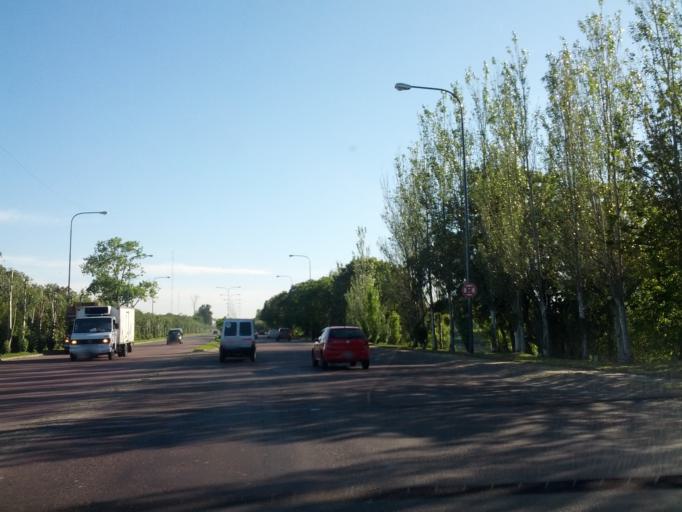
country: AR
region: Buenos Aires F.D.
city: Villa Lugano
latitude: -34.6798
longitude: -58.4402
